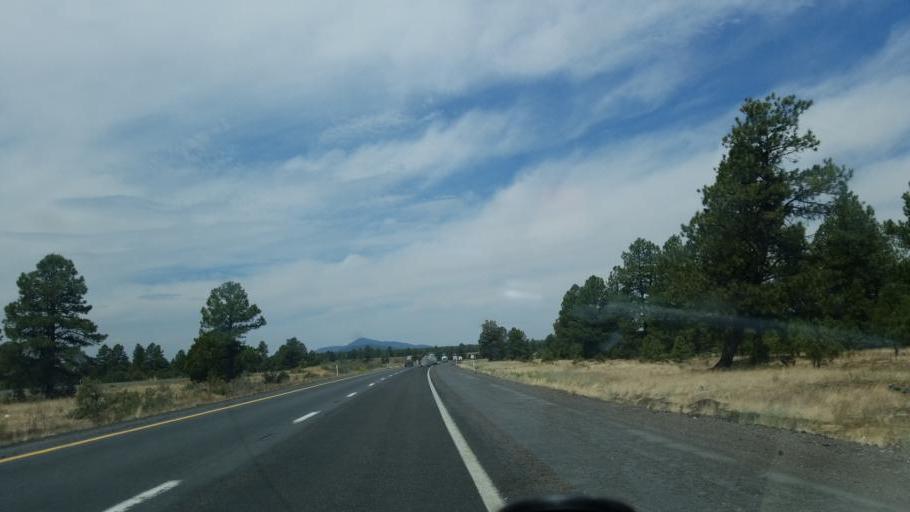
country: US
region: Arizona
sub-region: Coconino County
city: Parks
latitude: 35.2485
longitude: -111.9706
